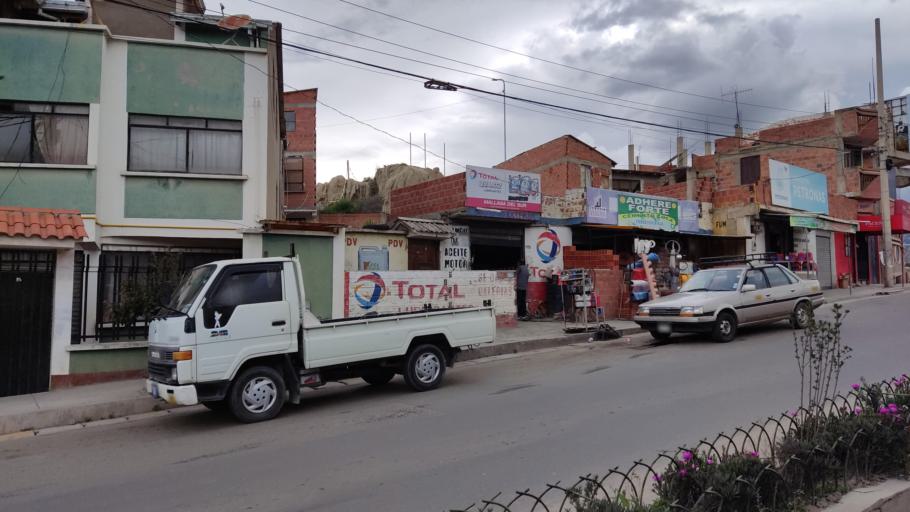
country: BO
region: La Paz
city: La Paz
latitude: -16.5673
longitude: -68.0913
